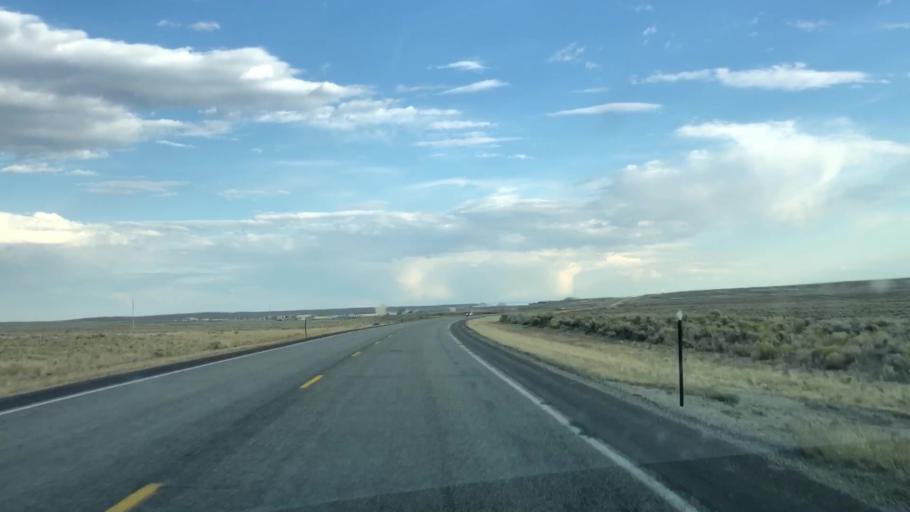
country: US
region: Wyoming
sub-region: Sublette County
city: Pinedale
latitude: 42.6202
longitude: -109.6510
